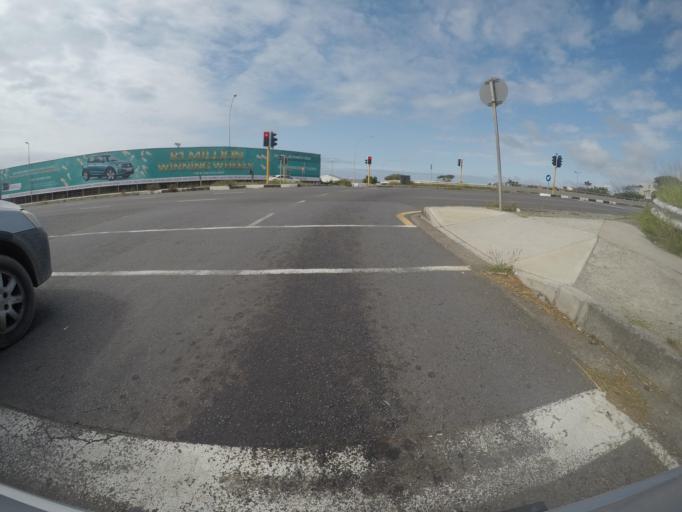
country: ZA
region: Eastern Cape
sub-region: Buffalo City Metropolitan Municipality
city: East London
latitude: -32.9932
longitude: 27.9186
